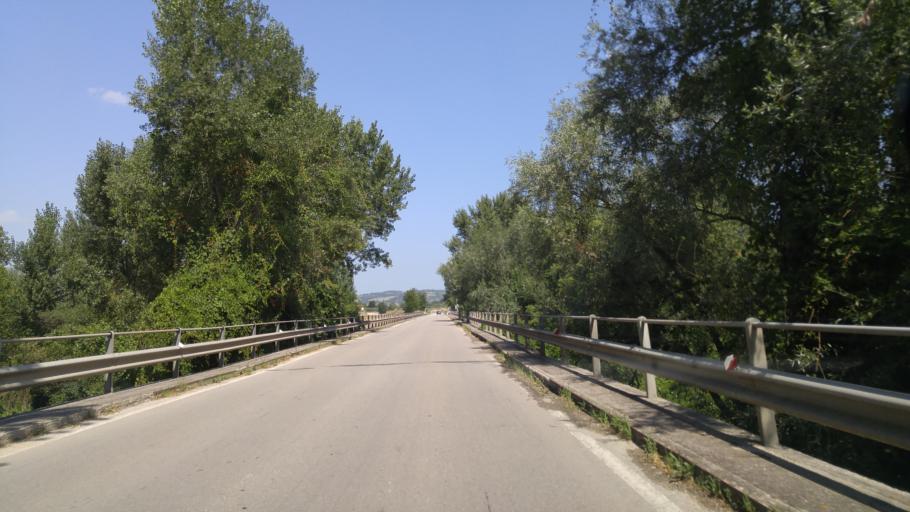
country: IT
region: The Marches
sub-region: Provincia di Pesaro e Urbino
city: Piagge
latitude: 43.7615
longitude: 12.9676
